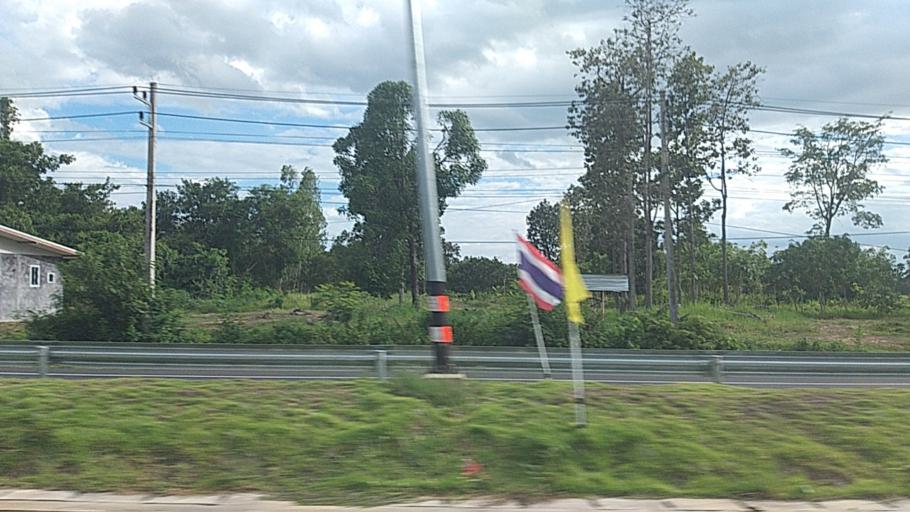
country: TH
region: Surin
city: Prasat
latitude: 14.5888
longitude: 103.4682
